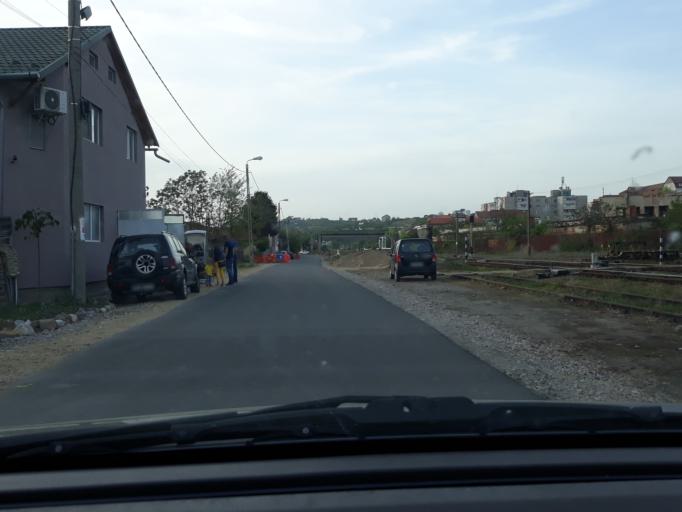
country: RO
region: Bihor
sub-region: Comuna Biharea
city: Oradea
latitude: 47.0449
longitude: 21.9617
